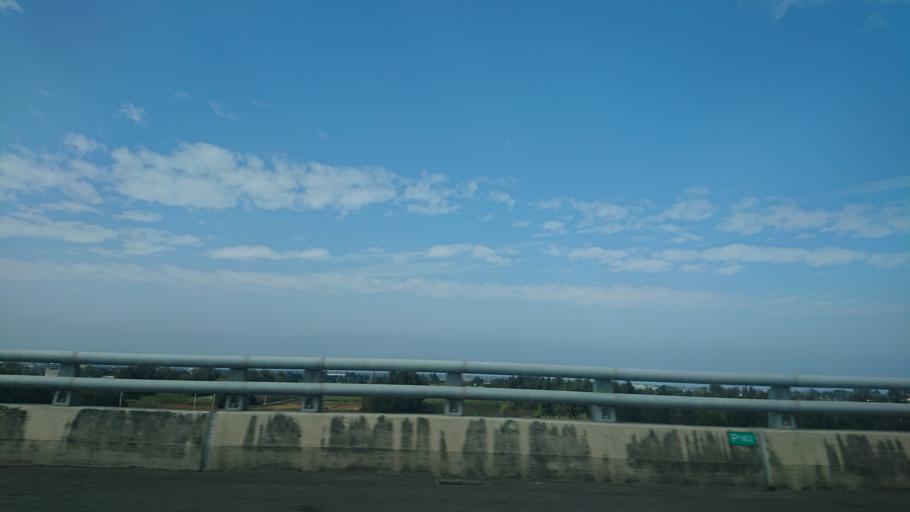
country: TW
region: Taiwan
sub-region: Yunlin
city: Douliu
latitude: 23.8516
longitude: 120.2953
